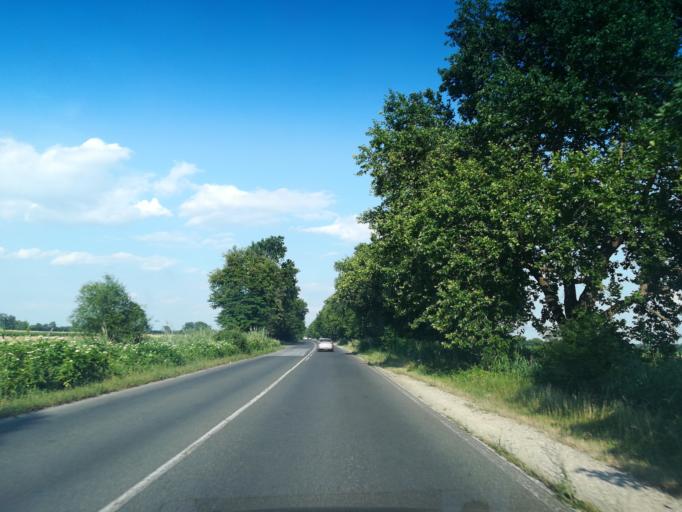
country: BG
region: Plovdiv
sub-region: Obshtina Sadovo
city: Sadovo
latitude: 42.1463
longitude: 24.8481
